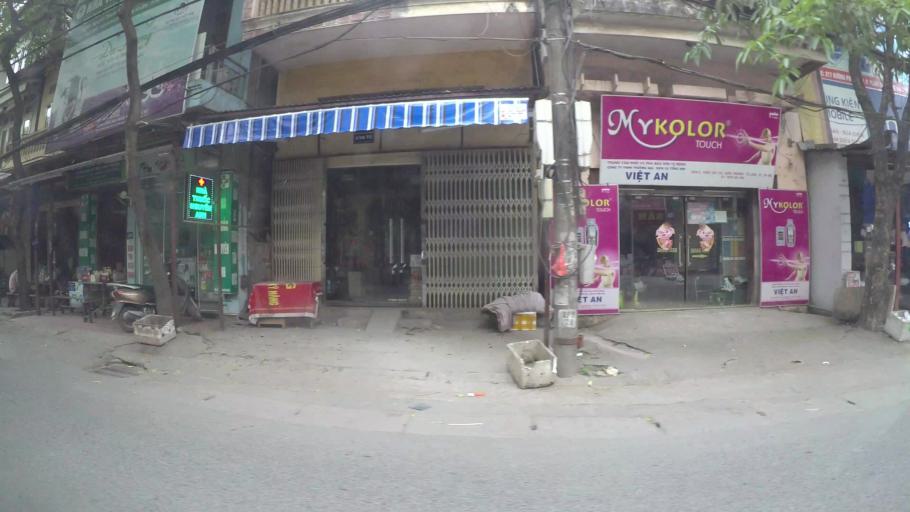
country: VN
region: Ha Noi
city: Cau Dien
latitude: 21.0376
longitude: 105.7580
